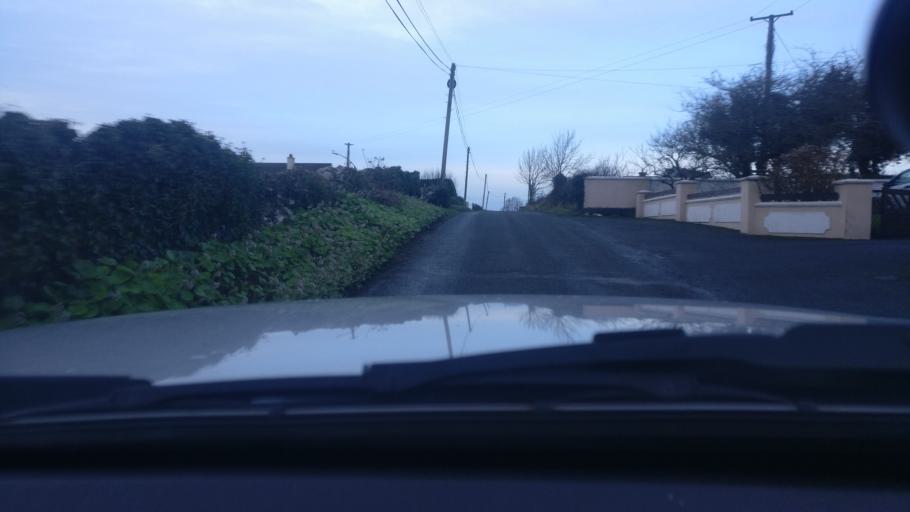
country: IE
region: Connaught
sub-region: County Galway
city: Loughrea
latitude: 53.1838
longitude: -8.5999
